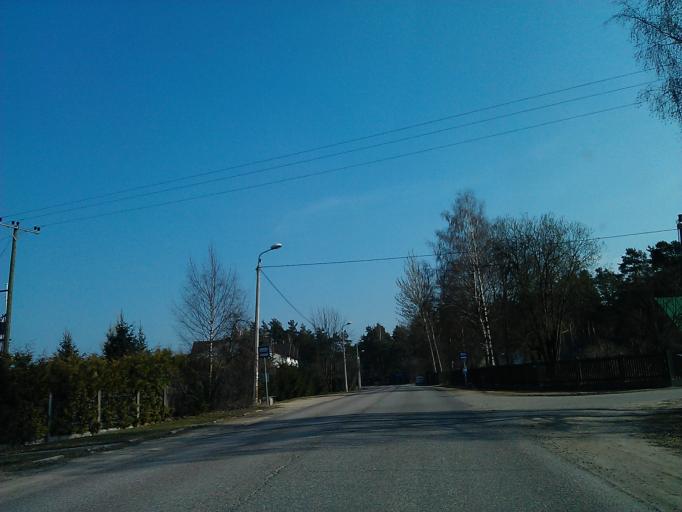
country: LV
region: Riga
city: Bergi
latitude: 56.9876
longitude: 24.3034
